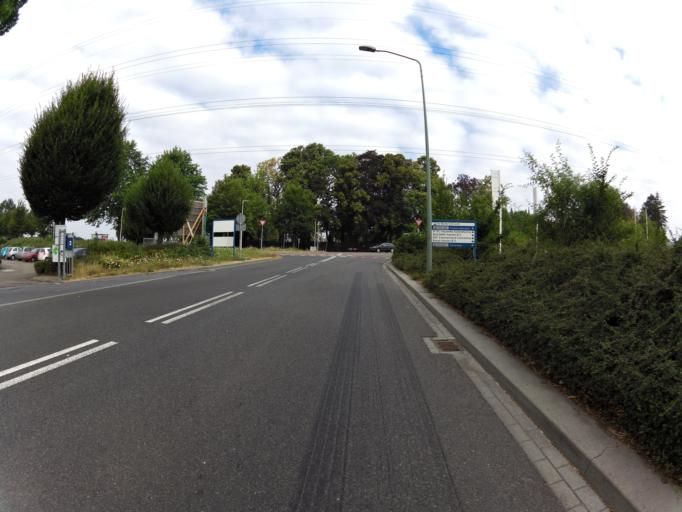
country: NL
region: Limburg
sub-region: Gemeente Simpelveld
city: Simpelveld
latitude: 50.8509
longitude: 5.9859
